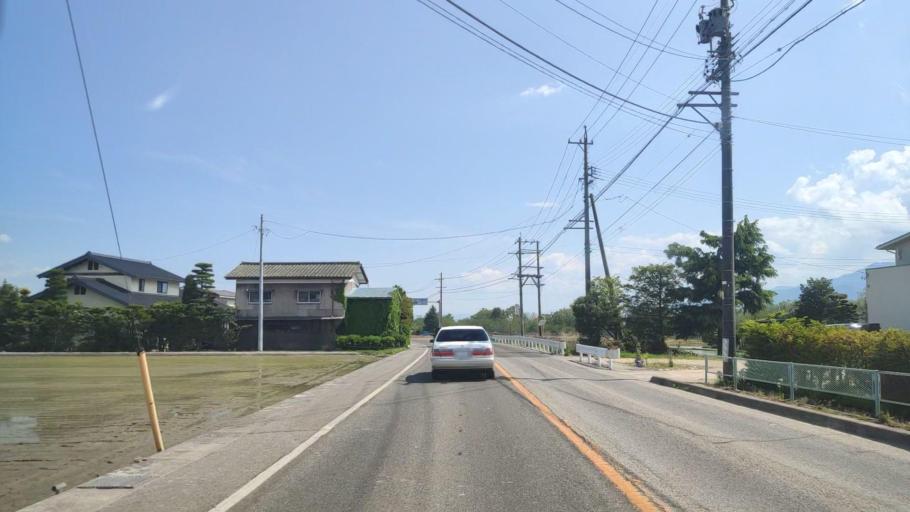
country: JP
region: Nagano
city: Hotaka
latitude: 36.3875
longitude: 137.8650
